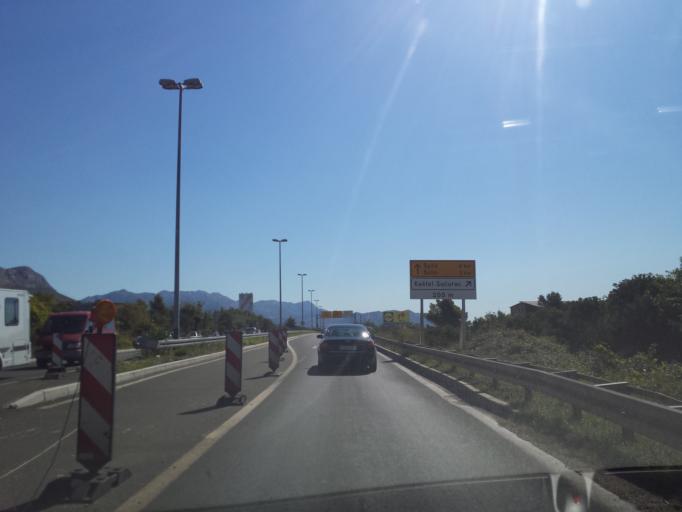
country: HR
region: Splitsko-Dalmatinska
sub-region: Grad Split
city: Split
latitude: 43.5531
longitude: 16.4057
